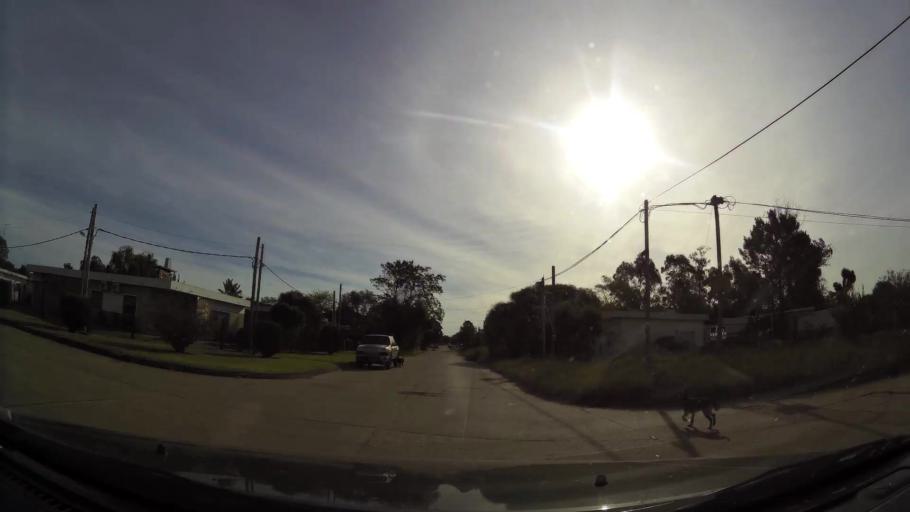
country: UY
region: Canelones
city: Atlantida
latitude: -34.7838
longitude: -55.8425
